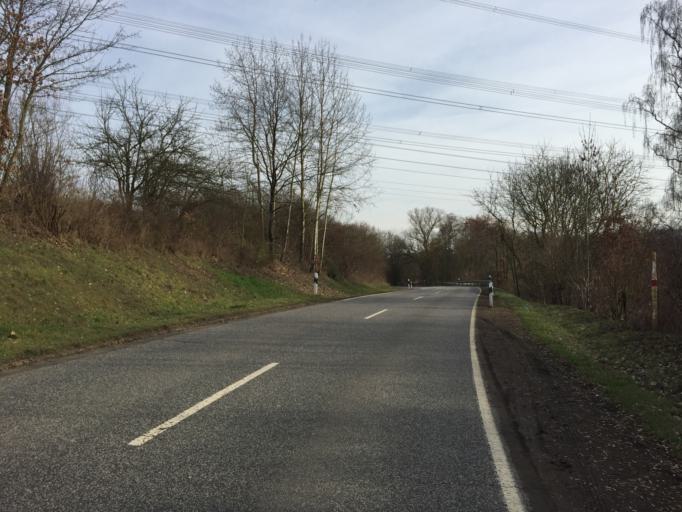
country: DE
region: Hesse
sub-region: Regierungsbezirk Giessen
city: Fronhausen
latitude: 50.6803
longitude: 8.6931
